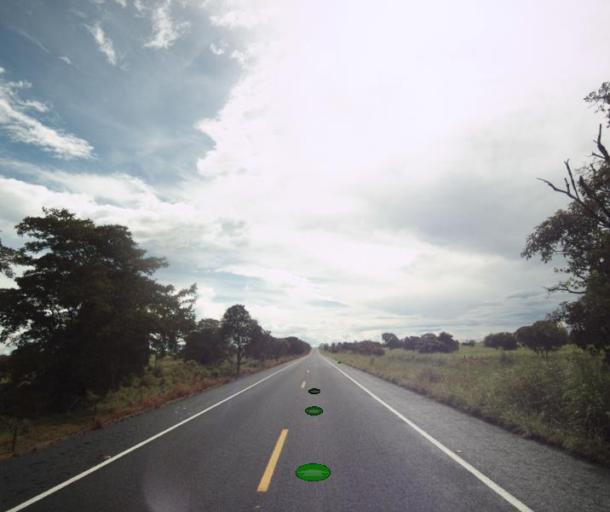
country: BR
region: Goias
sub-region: Sao Miguel Do Araguaia
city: Sao Miguel do Araguaia
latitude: -13.2912
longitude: -50.4151
